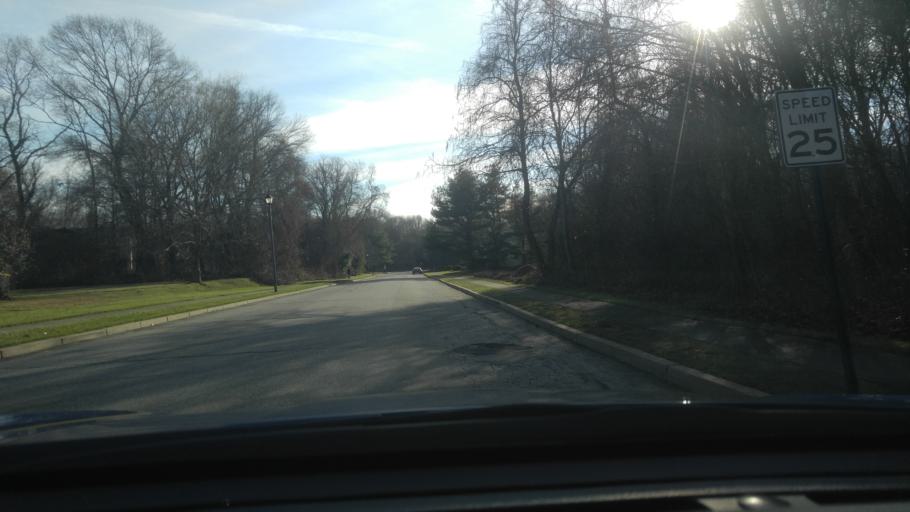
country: US
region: Rhode Island
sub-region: Kent County
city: East Greenwich
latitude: 41.6825
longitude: -71.4691
